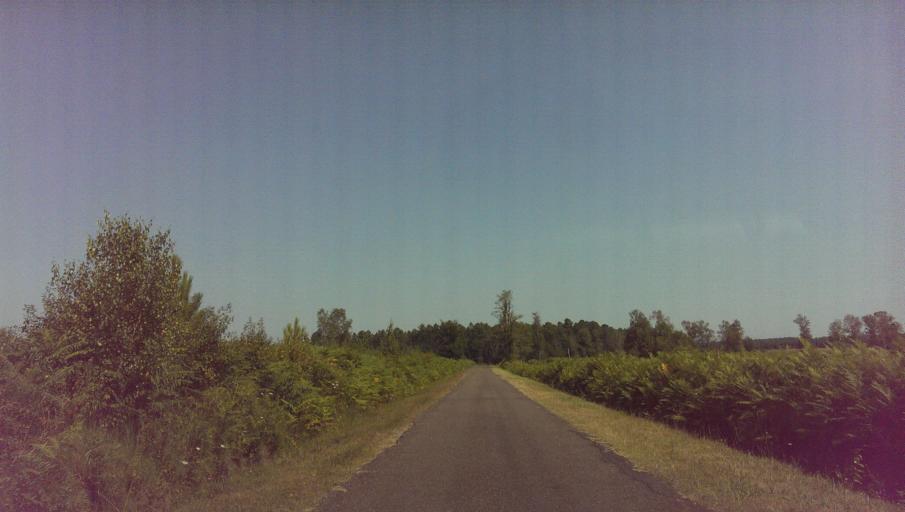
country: FR
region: Aquitaine
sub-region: Departement des Landes
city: Sarbazan
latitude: 44.0197
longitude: -0.1958
